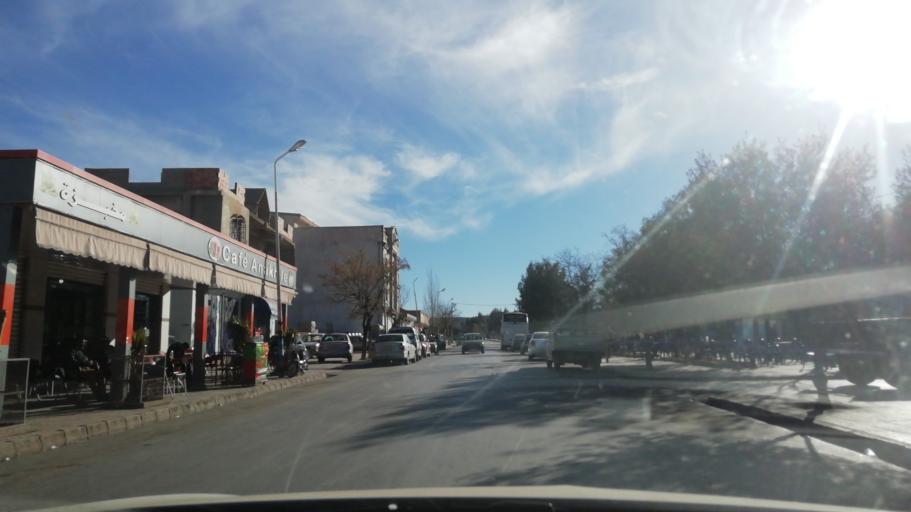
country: DZ
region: Tlemcen
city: Sebdou
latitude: 34.6303
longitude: -1.3334
